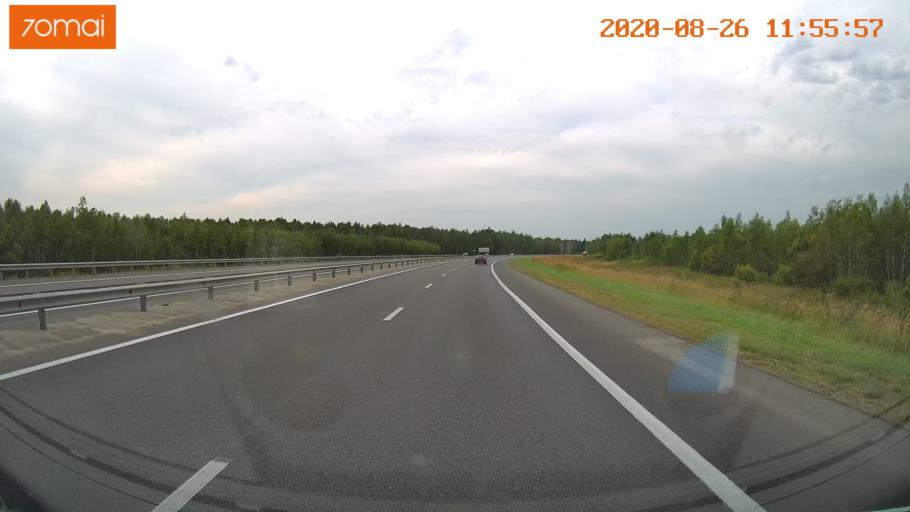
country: RU
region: Rjazan
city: Kiritsy
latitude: 54.2665
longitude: 40.3874
